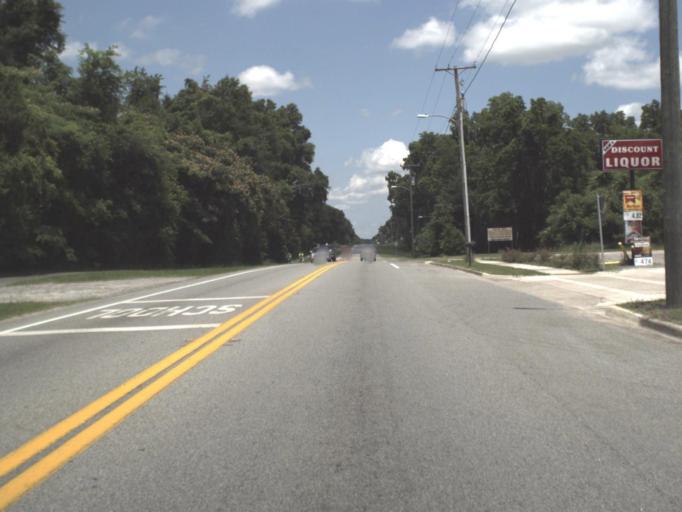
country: US
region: Florida
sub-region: Alachua County
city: High Springs
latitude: 29.9242
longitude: -82.7177
